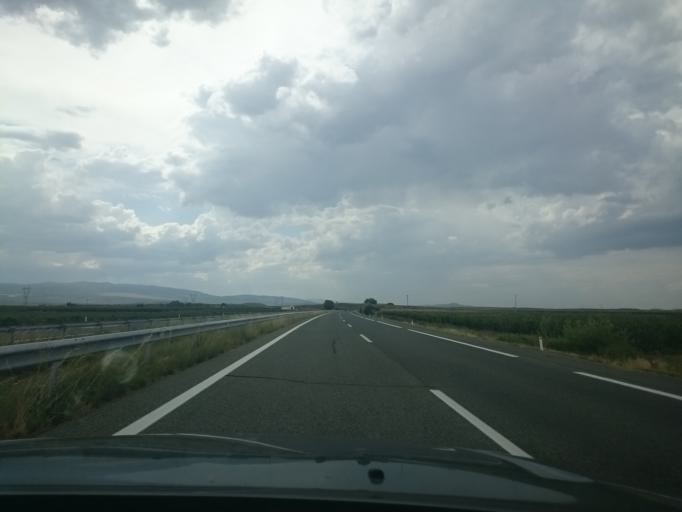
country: ES
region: Navarre
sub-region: Provincia de Navarra
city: Corella
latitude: 42.1519
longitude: -1.8014
